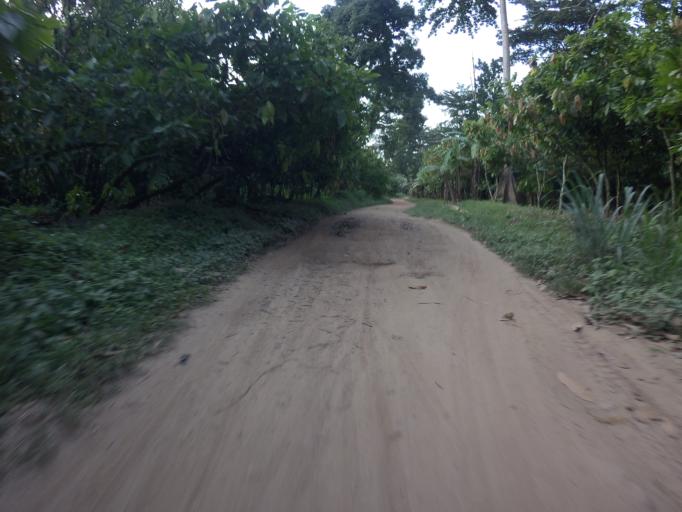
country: GH
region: Volta
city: Kpandu
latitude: 6.8851
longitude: 0.4370
